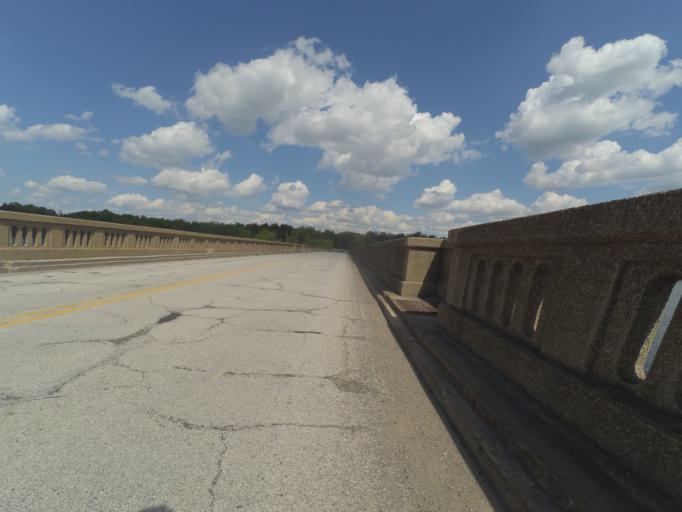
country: US
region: Ohio
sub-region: Trumbull County
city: Mineral Ridge
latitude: 41.1353
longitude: -80.7941
